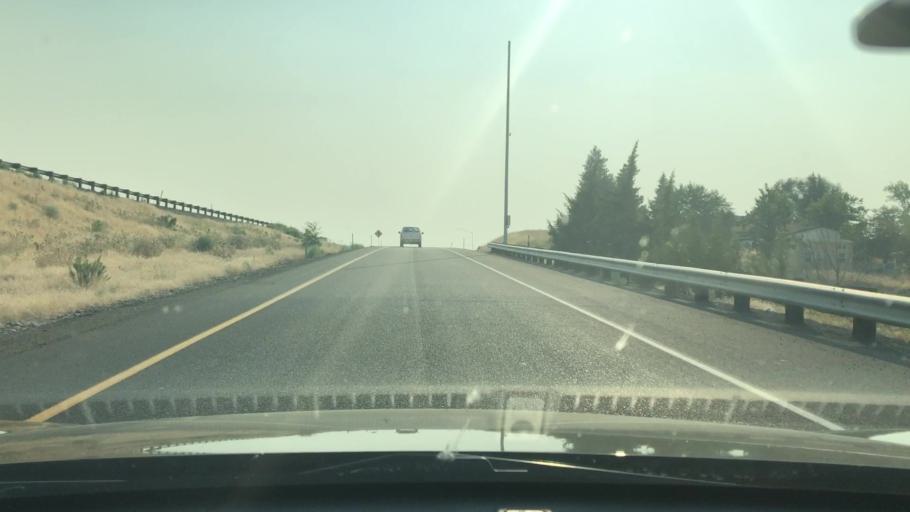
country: US
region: Oregon
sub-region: Umatilla County
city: Pendleton
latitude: 45.6637
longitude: -118.7791
